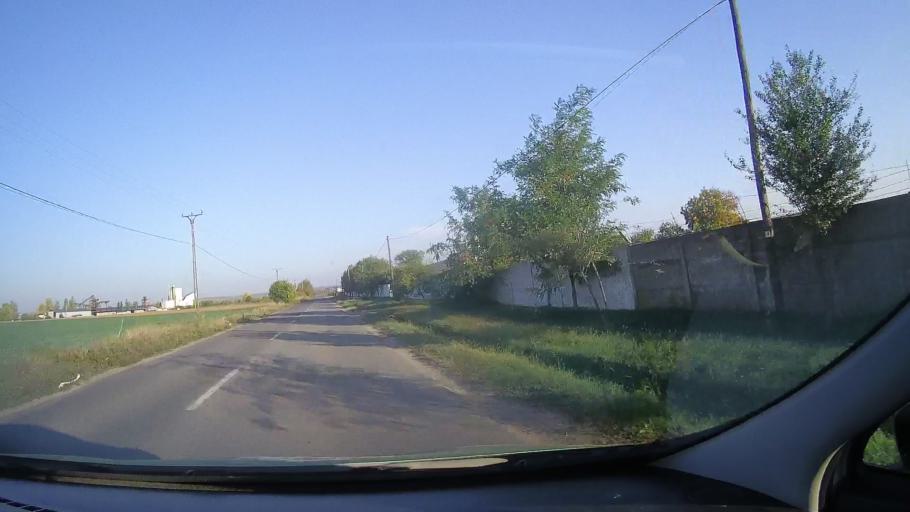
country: RO
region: Bihor
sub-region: Comuna Bors
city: Santion
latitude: 47.1138
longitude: 21.8490
